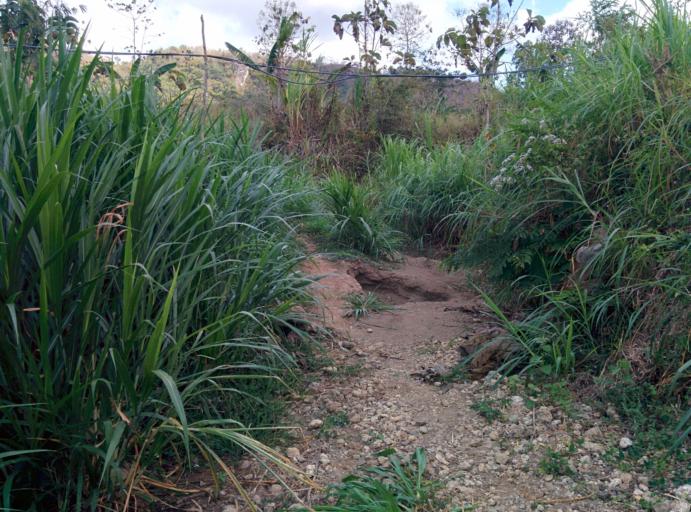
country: ID
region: East Java
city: Bacem
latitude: -8.2032
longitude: 112.2434
